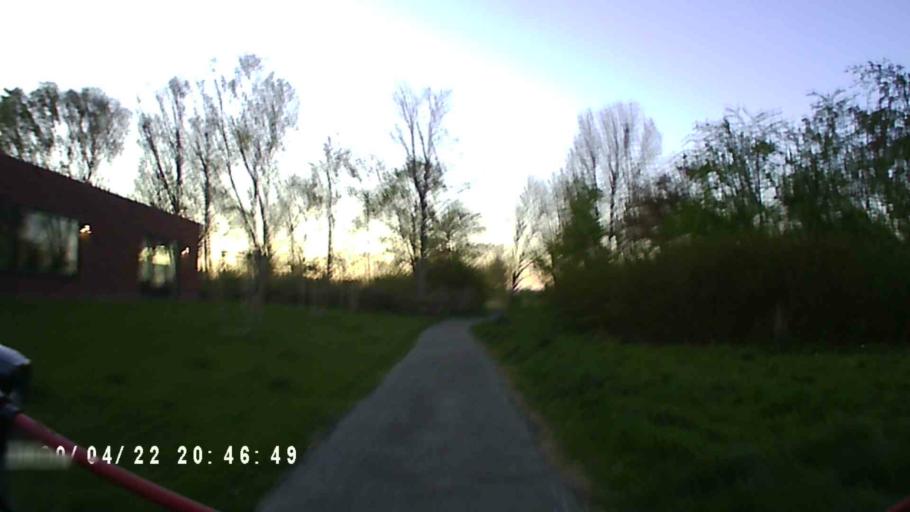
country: NL
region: Groningen
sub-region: Gemeente Winsum
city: Winsum
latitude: 53.3287
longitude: 6.5303
